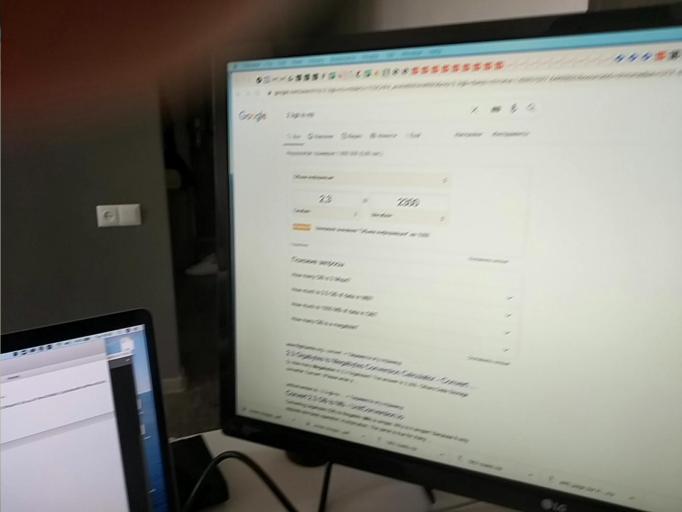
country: RU
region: Moskovskaya
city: Balashikha
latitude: 55.7953
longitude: 37.9615
